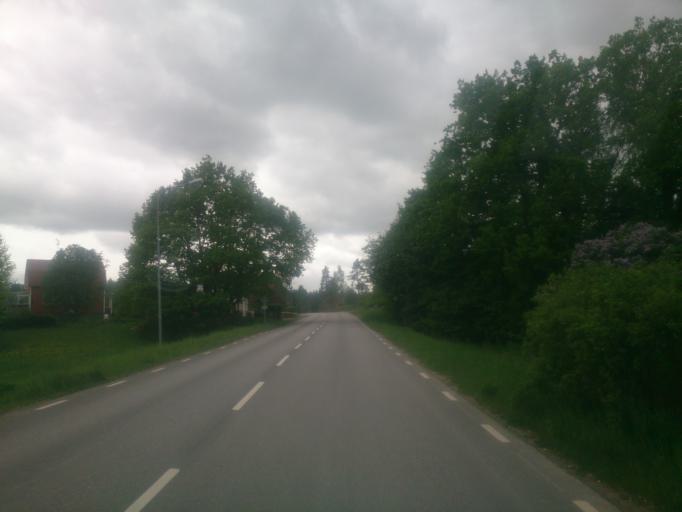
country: SE
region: OEstergoetland
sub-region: Atvidabergs Kommun
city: Atvidaberg
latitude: 58.2202
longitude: 16.0250
